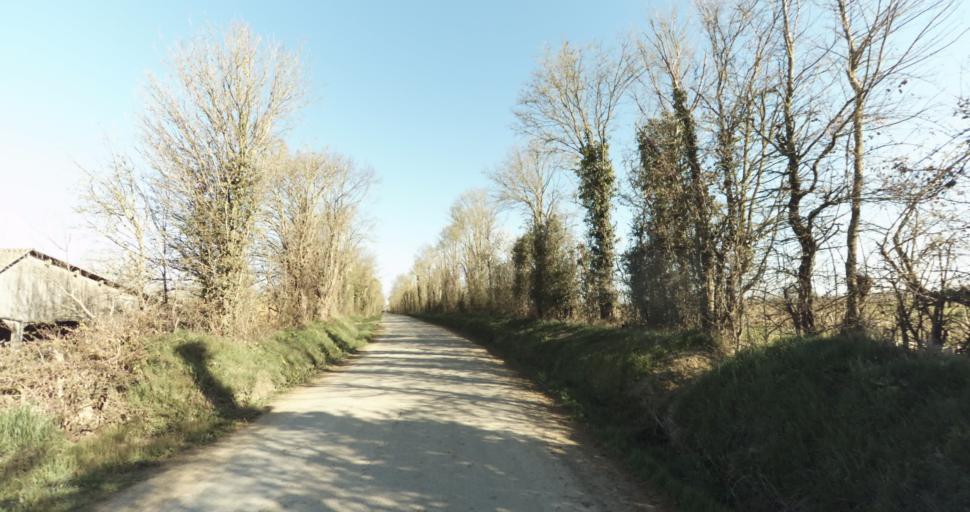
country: FR
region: Lower Normandy
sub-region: Departement du Calvados
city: Saint-Pierre-sur-Dives
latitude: 48.9934
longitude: -0.0015
